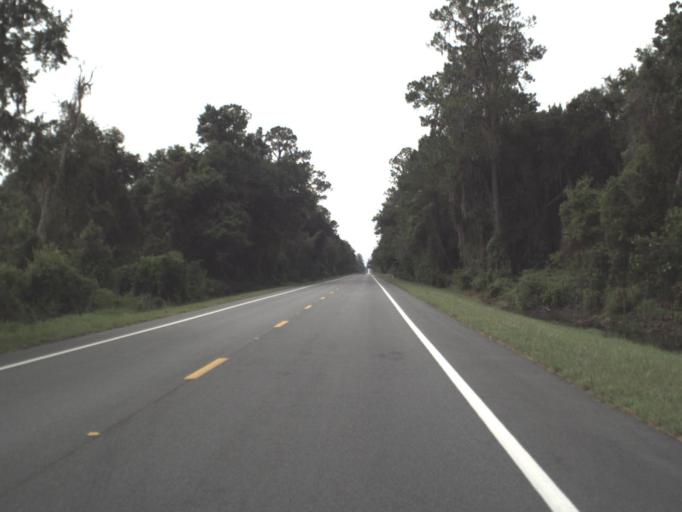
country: US
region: Florida
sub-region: Hamilton County
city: Jasper
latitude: 30.5335
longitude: -82.6767
